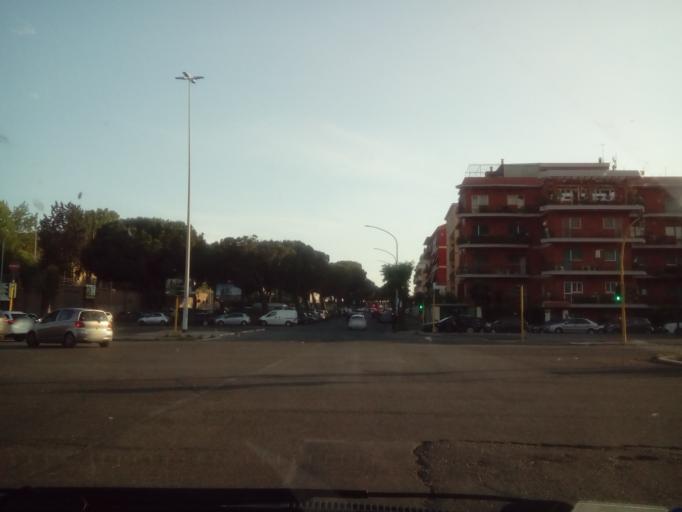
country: IT
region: Latium
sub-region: Citta metropolitana di Roma Capitale
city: Ciampino
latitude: 41.8527
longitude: 12.5698
